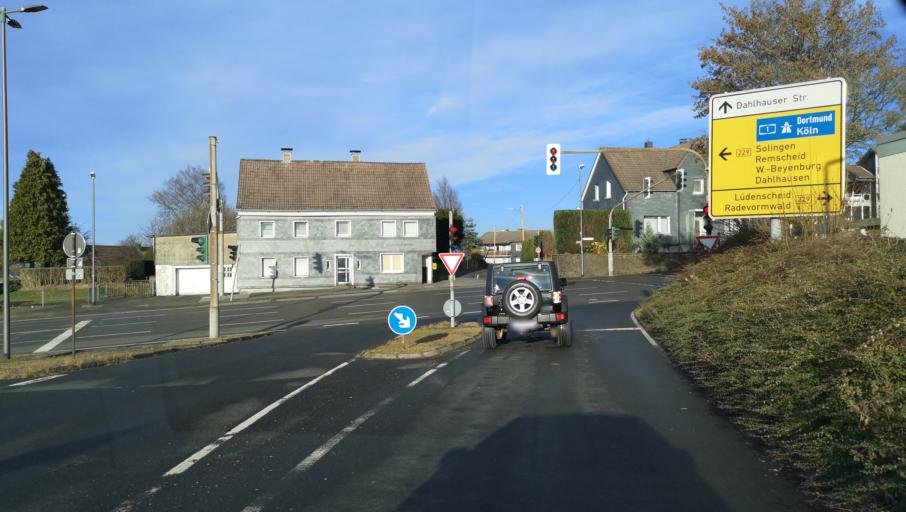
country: DE
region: North Rhine-Westphalia
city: Radevormwald
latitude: 51.2016
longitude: 7.3210
